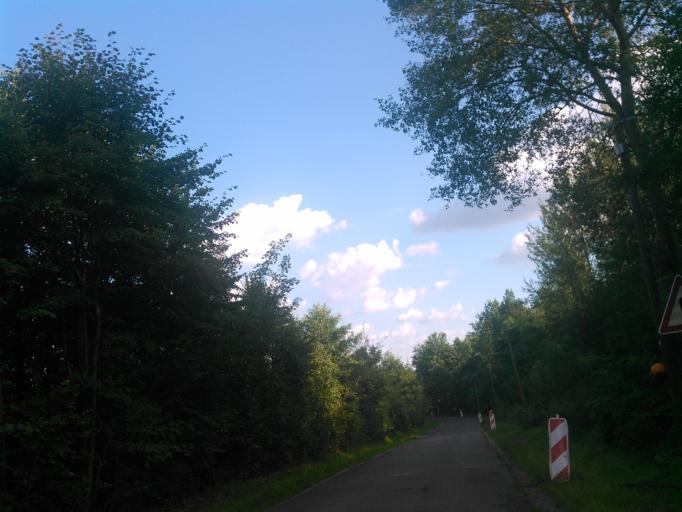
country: DE
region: Saarland
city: Nalbach
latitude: 49.3944
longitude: 6.7869
